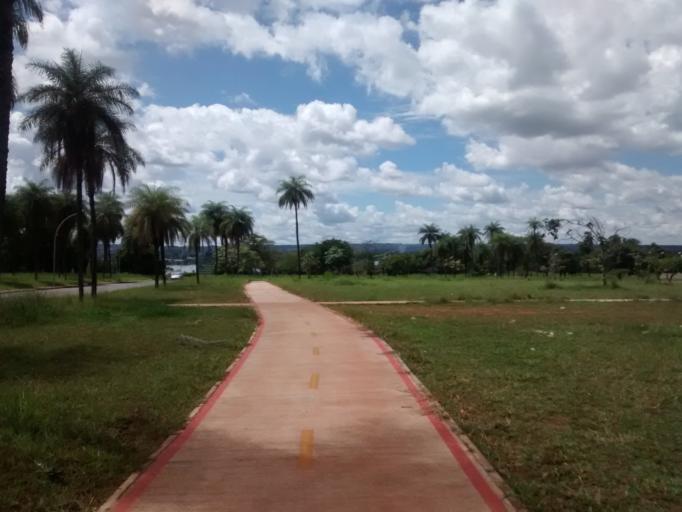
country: BR
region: Federal District
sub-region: Brasilia
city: Brasilia
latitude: -15.7599
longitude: -47.8695
